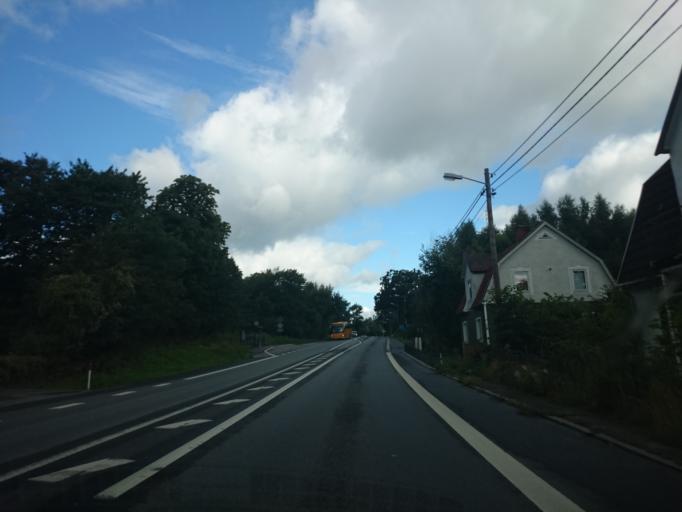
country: SE
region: Skane
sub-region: Kristianstads Kommun
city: Onnestad
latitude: 55.9404
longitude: 13.9056
